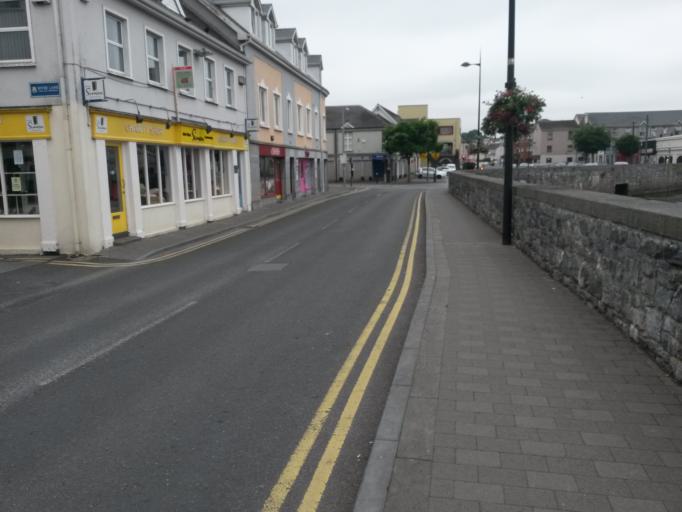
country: IE
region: Munster
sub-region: An Clar
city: Ennis
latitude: 52.8442
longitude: -8.9864
